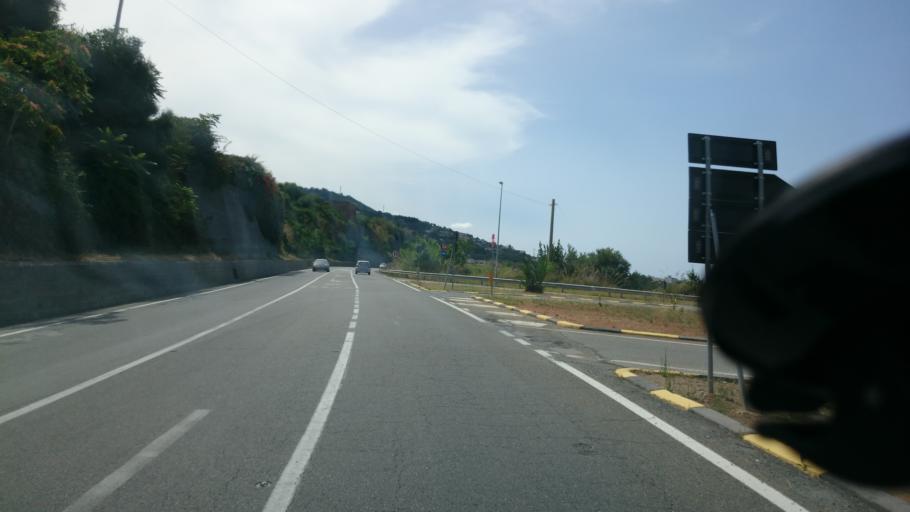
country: IT
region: Calabria
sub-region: Provincia di Cosenza
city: Diamante
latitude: 39.7130
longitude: 15.8119
